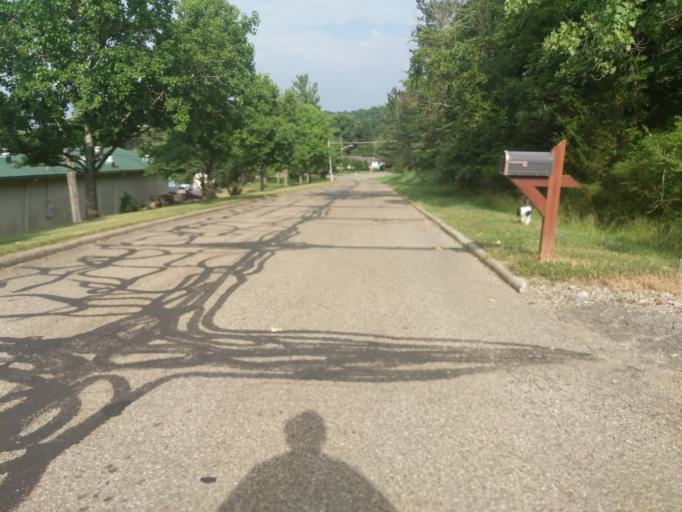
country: US
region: Ohio
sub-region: Athens County
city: Athens
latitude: 39.3387
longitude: -82.0834
